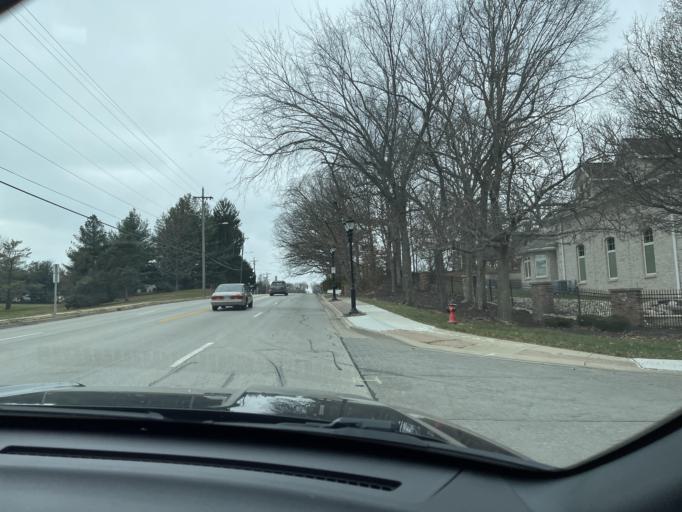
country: US
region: Illinois
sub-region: Sangamon County
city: Leland Grove
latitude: 39.7941
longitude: -89.6849
